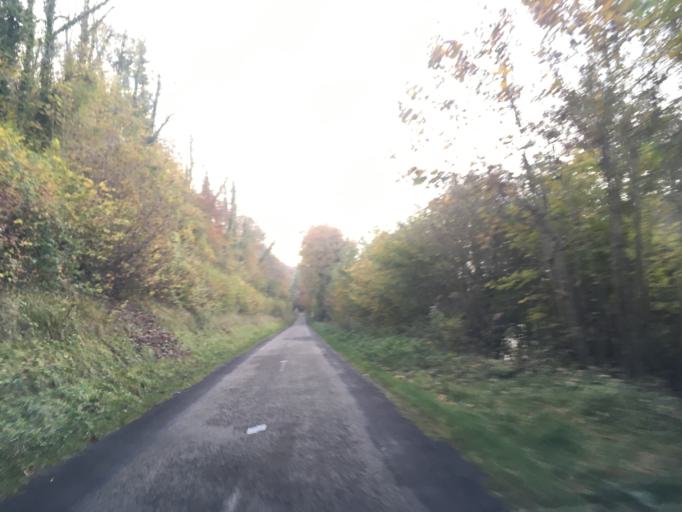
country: FR
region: Haute-Normandie
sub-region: Departement de l'Eure
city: Heudreville-sur-Eure
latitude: 49.1089
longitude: 1.2163
